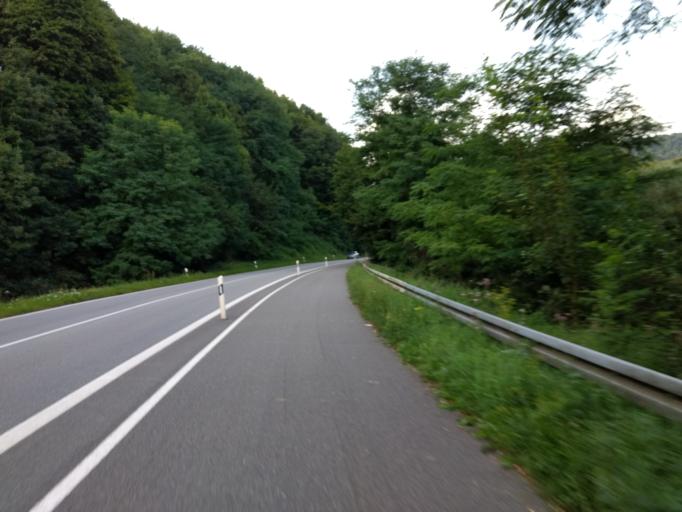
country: DE
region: Saarland
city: Rehlingen-Siersburg
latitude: 49.3867
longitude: 6.6649
